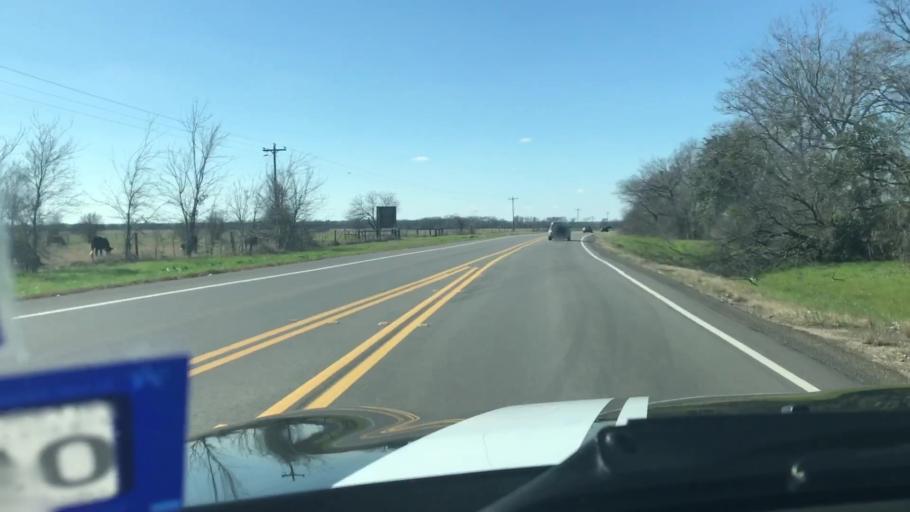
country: US
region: Texas
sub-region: Robertson County
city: Hearne
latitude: 30.8836
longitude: -96.6284
